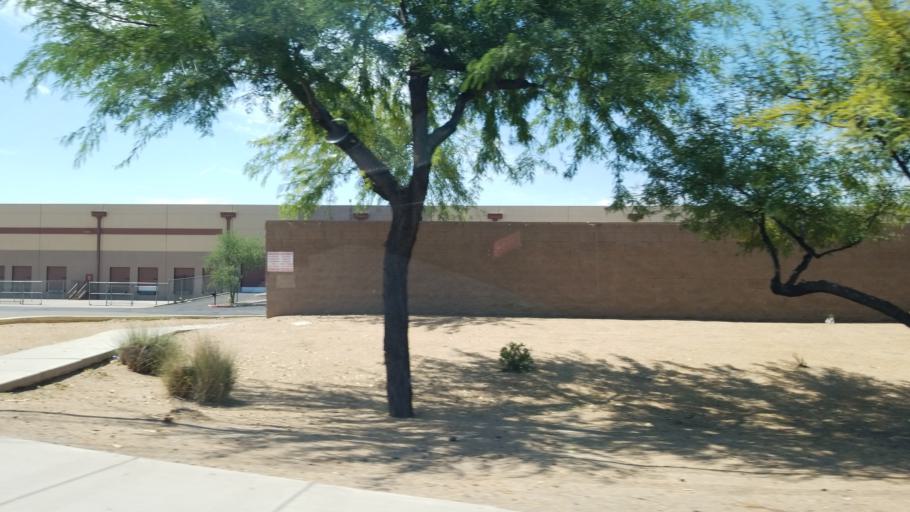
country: US
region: Arizona
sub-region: Maricopa County
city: Laveen
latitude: 33.4368
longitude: -112.1584
